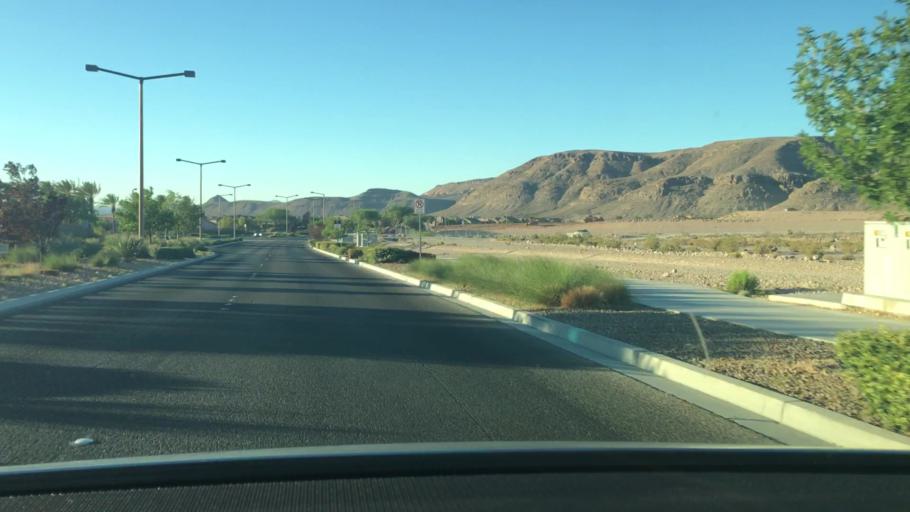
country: US
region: Nevada
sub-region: Clark County
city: Summerlin South
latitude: 36.0958
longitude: -115.3252
